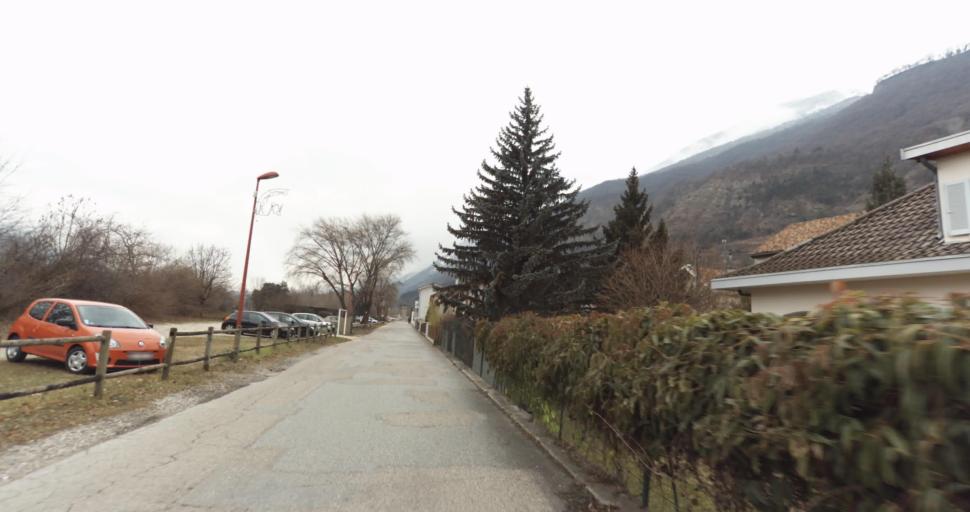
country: FR
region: Rhone-Alpes
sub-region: Departement de l'Isere
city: Vif
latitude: 45.0546
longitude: 5.6665
